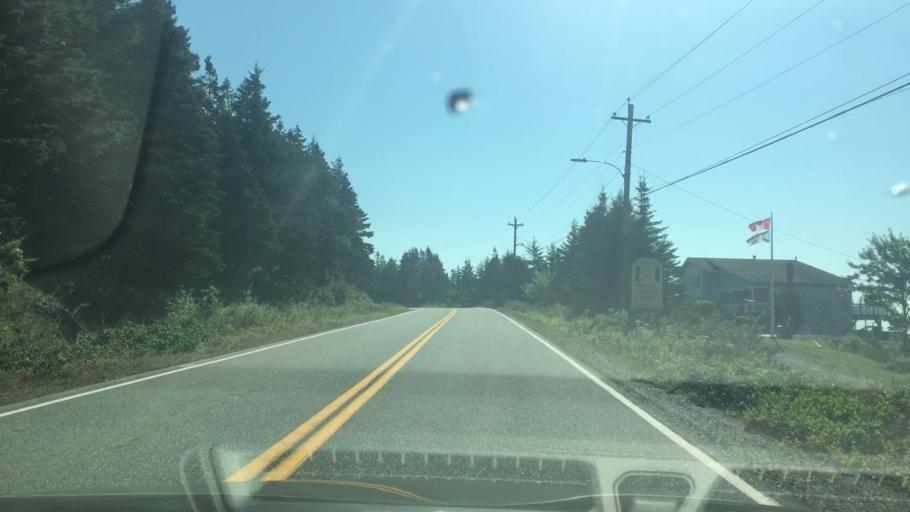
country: CA
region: Nova Scotia
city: New Glasgow
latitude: 44.8044
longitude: -62.7048
